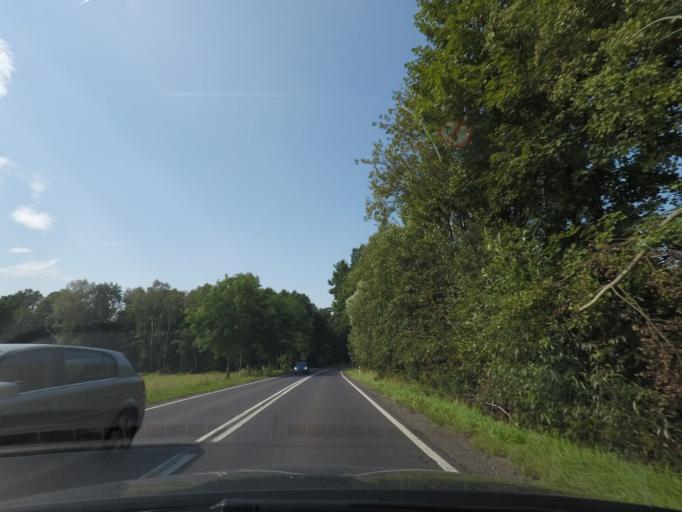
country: PL
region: Lesser Poland Voivodeship
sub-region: Powiat chrzanowski
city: Libiaz
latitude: 50.0842
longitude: 19.2866
